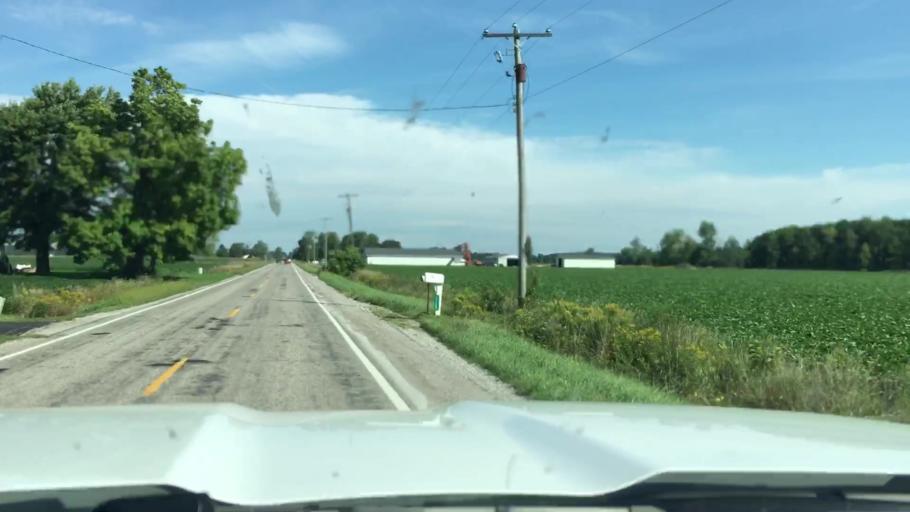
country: US
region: Michigan
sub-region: Saginaw County
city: Hemlock
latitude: 43.4327
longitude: -84.2299
